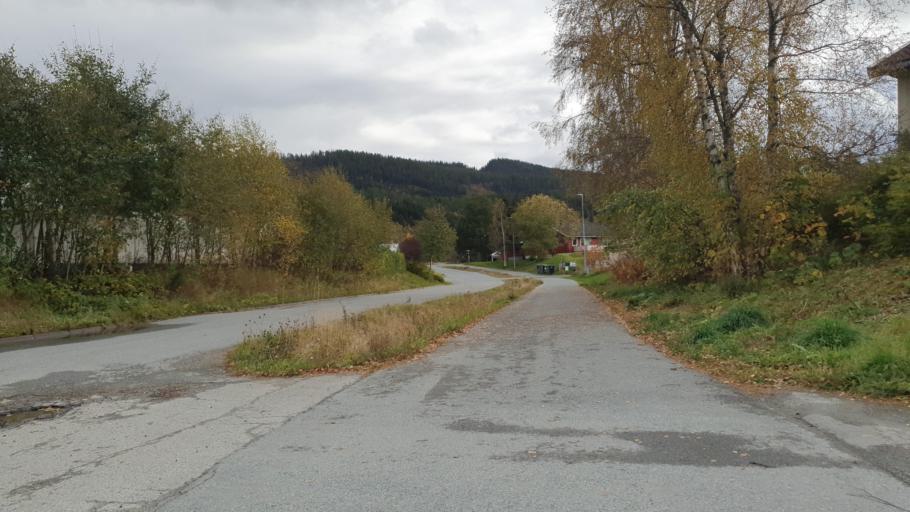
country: NO
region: Sor-Trondelag
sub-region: Klaebu
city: Klaebu
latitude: 63.3044
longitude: 10.4795
